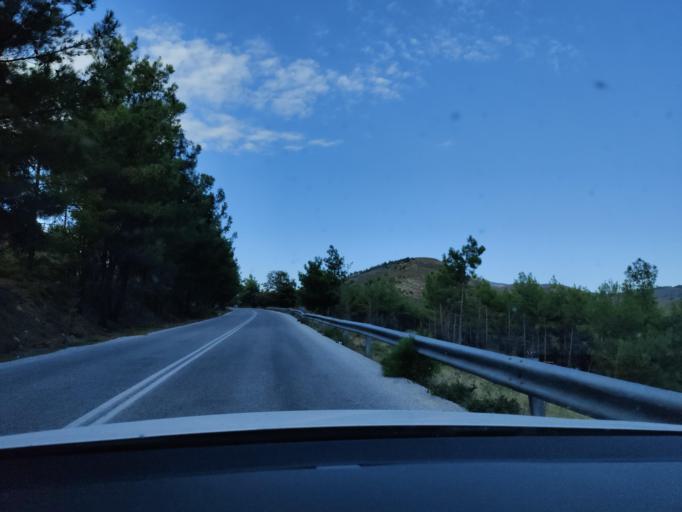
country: GR
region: East Macedonia and Thrace
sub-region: Nomos Kavalas
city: Limenaria
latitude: 40.6199
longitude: 24.6560
